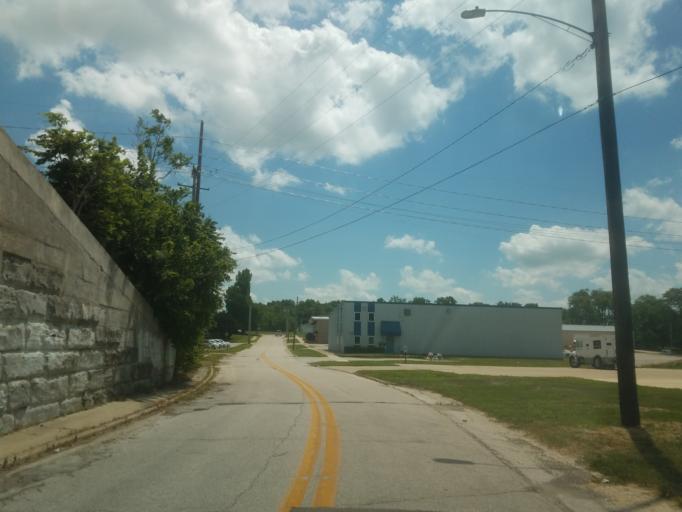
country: US
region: Illinois
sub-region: McLean County
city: Bloomington
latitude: 40.4810
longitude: -89.0136
